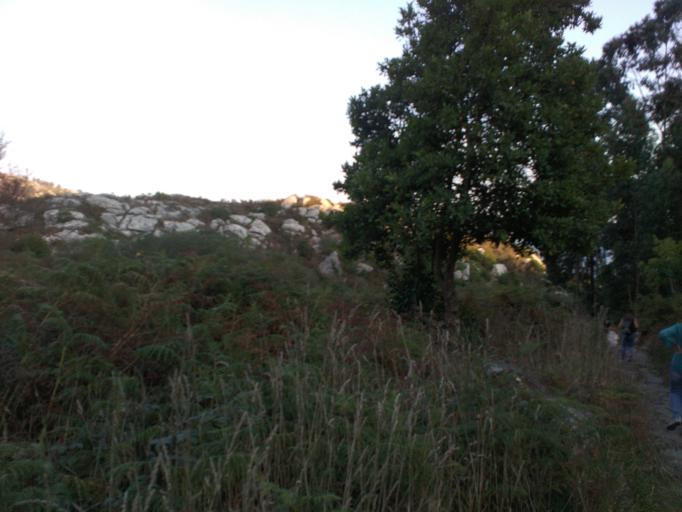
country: ES
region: Galicia
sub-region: Provincia de Pontevedra
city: Cangas
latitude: 42.2765
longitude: -8.8596
